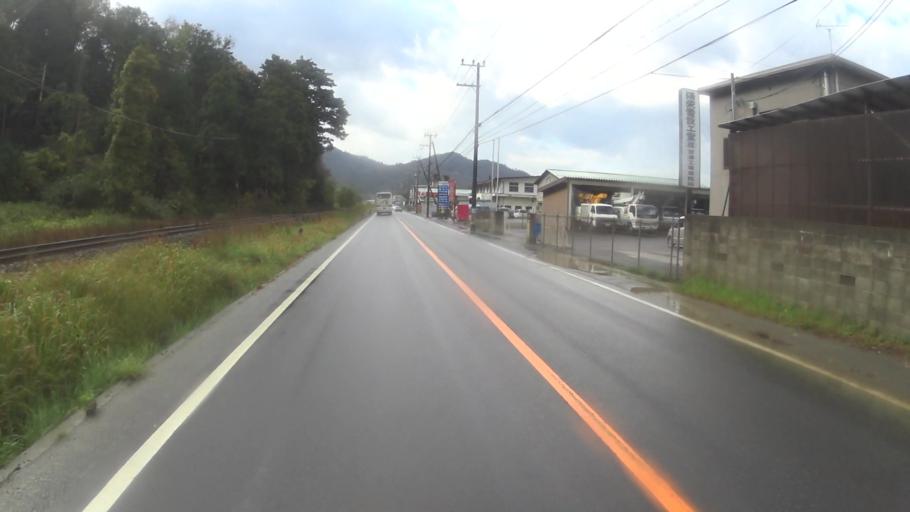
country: JP
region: Kyoto
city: Miyazu
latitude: 35.5591
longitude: 135.1657
